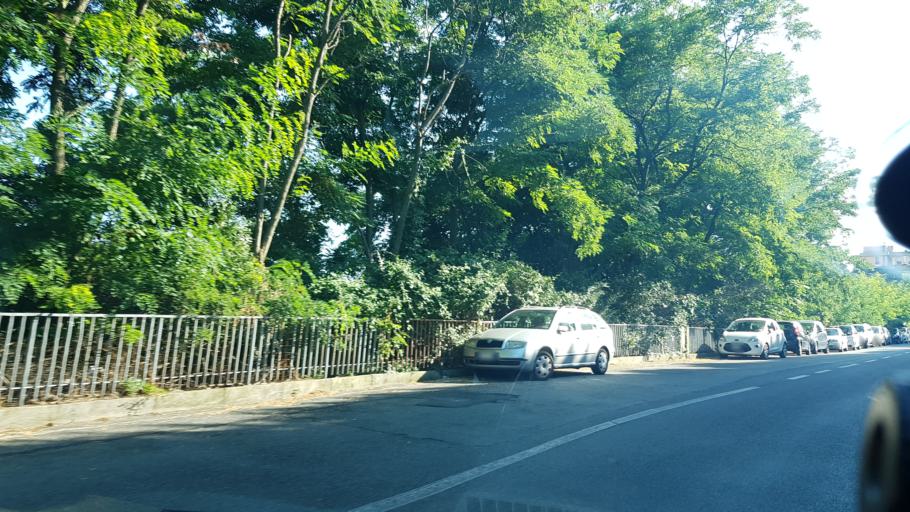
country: IT
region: Liguria
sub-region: Provincia di Genova
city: Genoa
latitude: 44.4412
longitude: 8.8986
